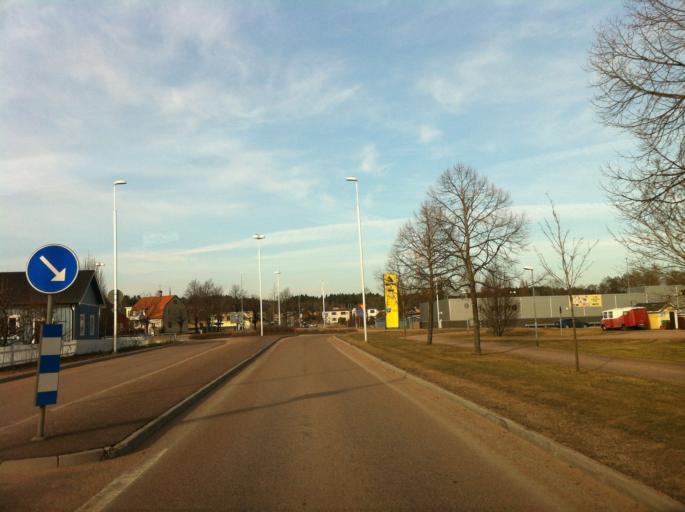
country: SE
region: Vaermland
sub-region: Kristinehamns Kommun
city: Kristinehamn
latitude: 59.3181
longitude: 14.1124
